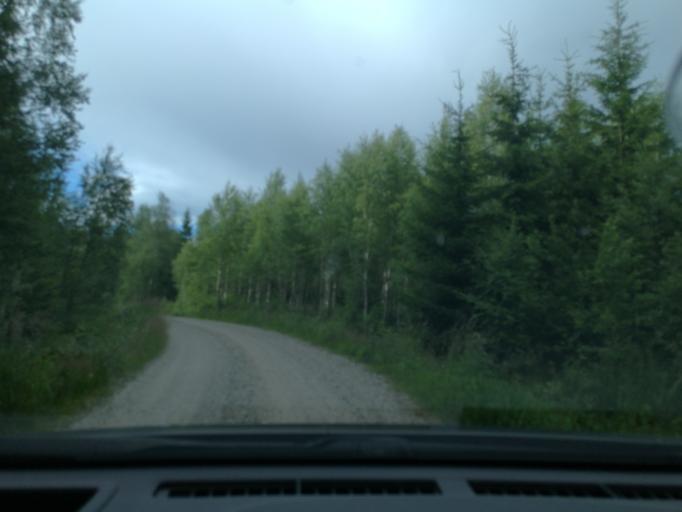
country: SE
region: Vaestmanland
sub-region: Surahammars Kommun
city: Ramnas
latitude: 59.8220
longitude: 16.2589
